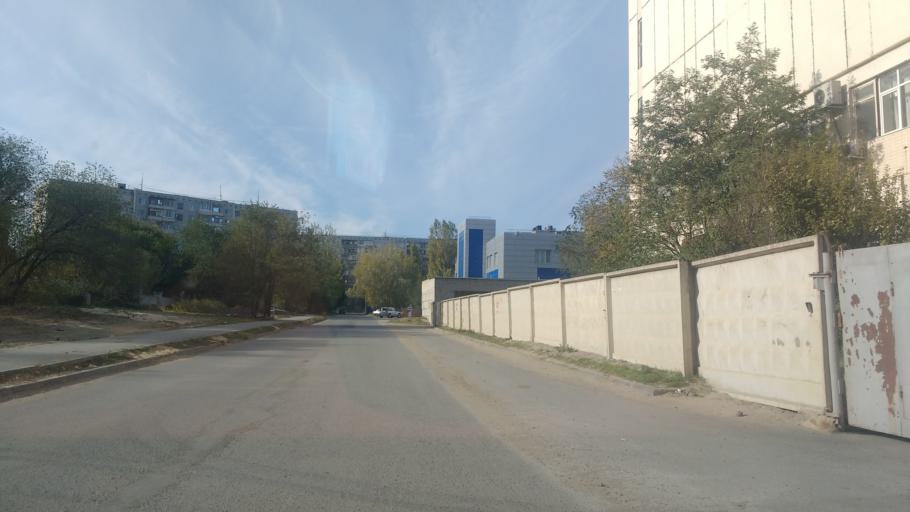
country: RU
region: Volgograd
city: Krasnoslobodsk
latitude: 48.7645
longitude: 44.5501
